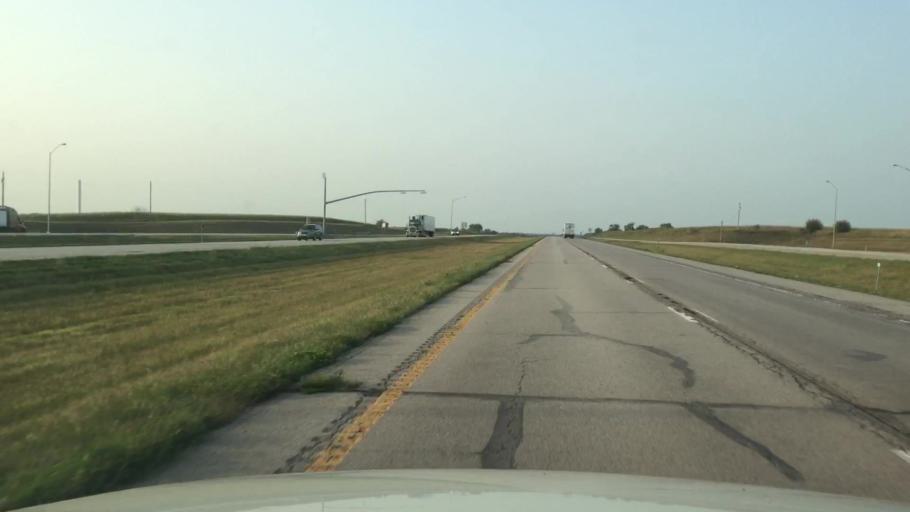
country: US
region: Iowa
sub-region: Decatur County
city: Lamoni
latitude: 40.5209
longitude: -93.9614
